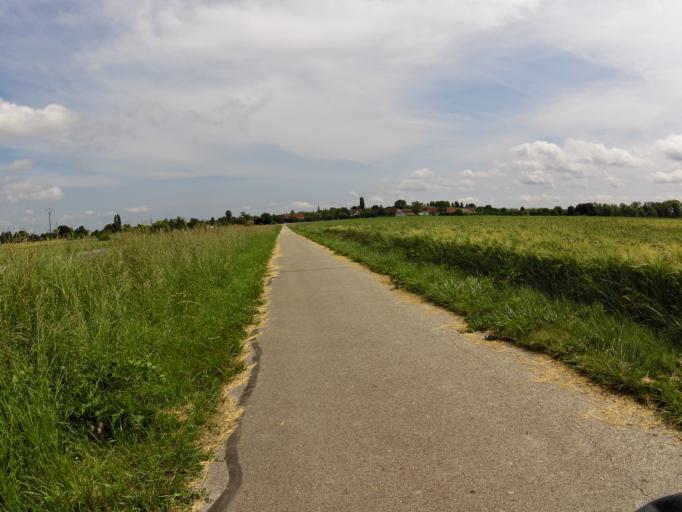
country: FR
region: Champagne-Ardenne
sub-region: Departement de l'Aube
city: Piney
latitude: 48.3036
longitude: 4.3124
